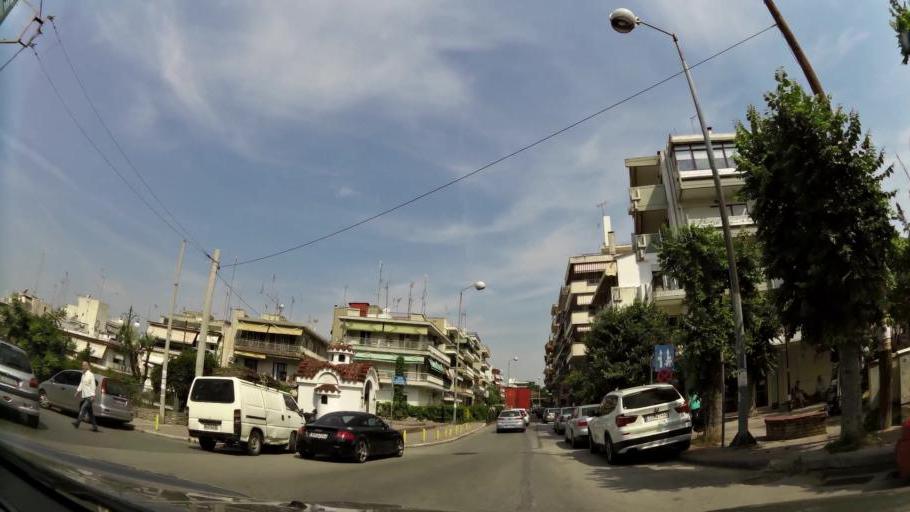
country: GR
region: Central Macedonia
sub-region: Nomos Thessalonikis
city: Thessaloniki
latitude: 40.6489
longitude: 22.9381
